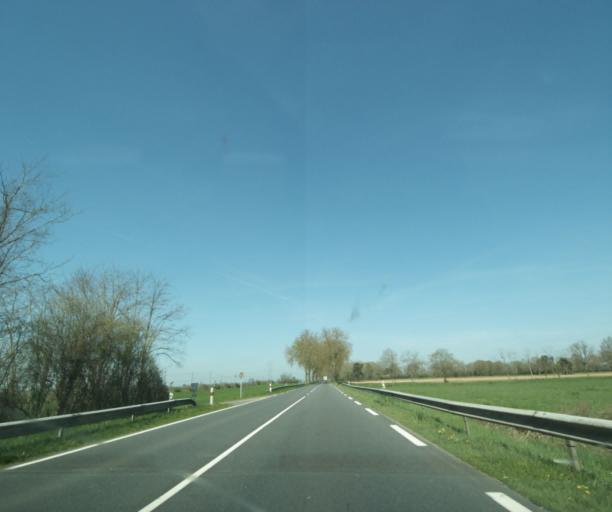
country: FR
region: Bourgogne
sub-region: Departement de la Nievre
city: Chantenay-Saint-Imbert
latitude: 46.6852
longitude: 3.2222
